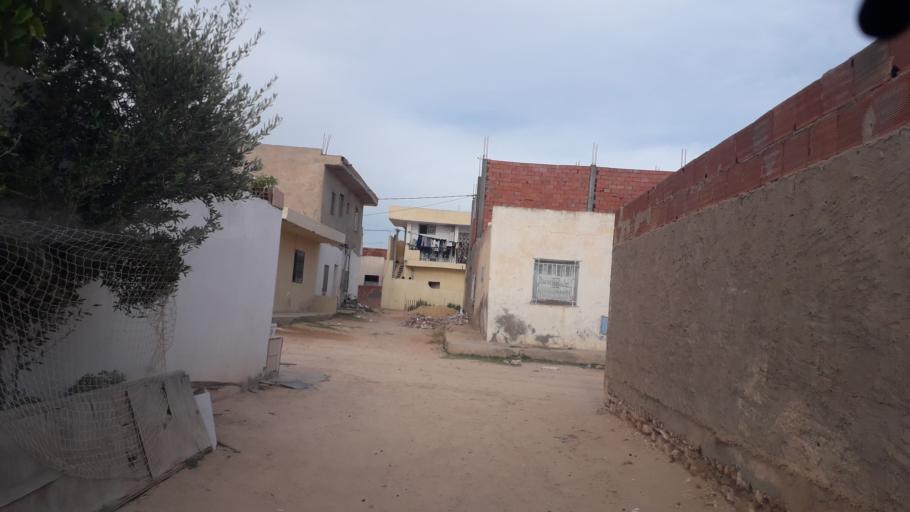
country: TN
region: Safaqis
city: Al Qarmadah
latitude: 34.8867
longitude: 10.7582
